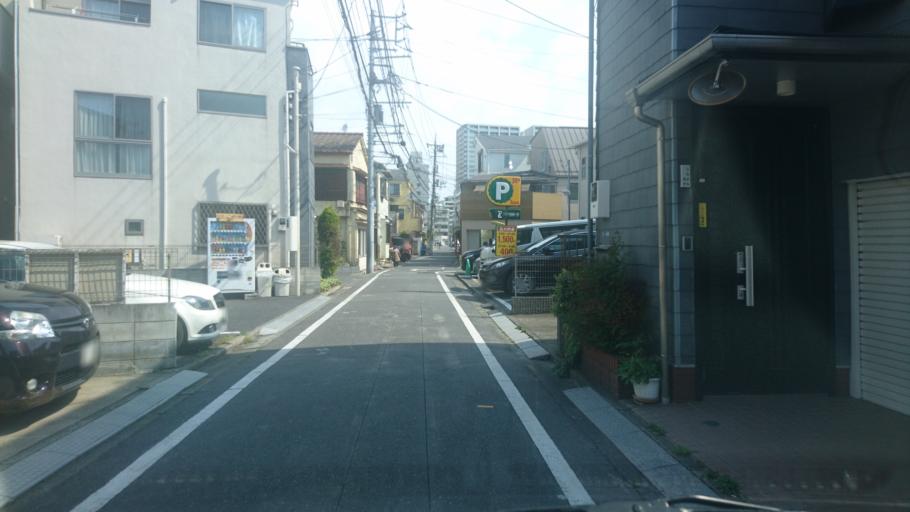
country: JP
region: Kanagawa
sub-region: Kawasaki-shi
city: Kawasaki
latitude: 35.5826
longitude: 139.7323
